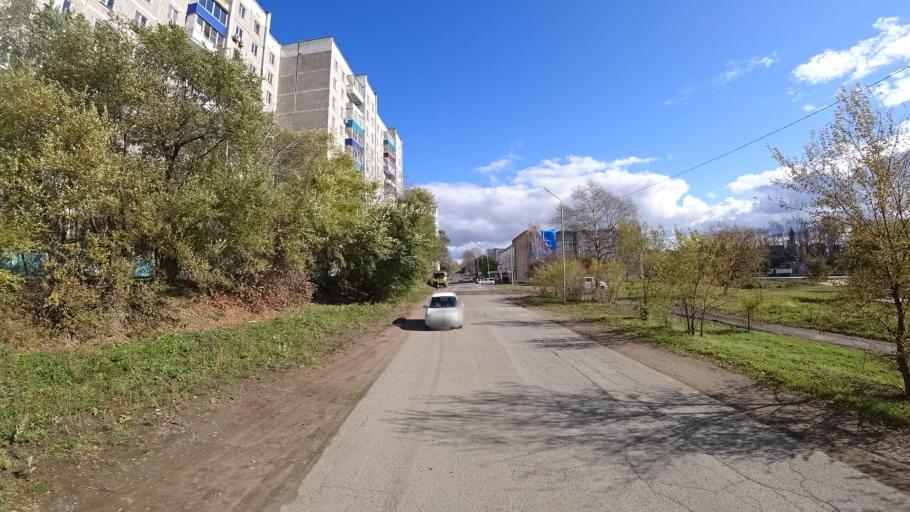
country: RU
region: Khabarovsk Krai
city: Amursk
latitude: 50.2148
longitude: 136.8942
